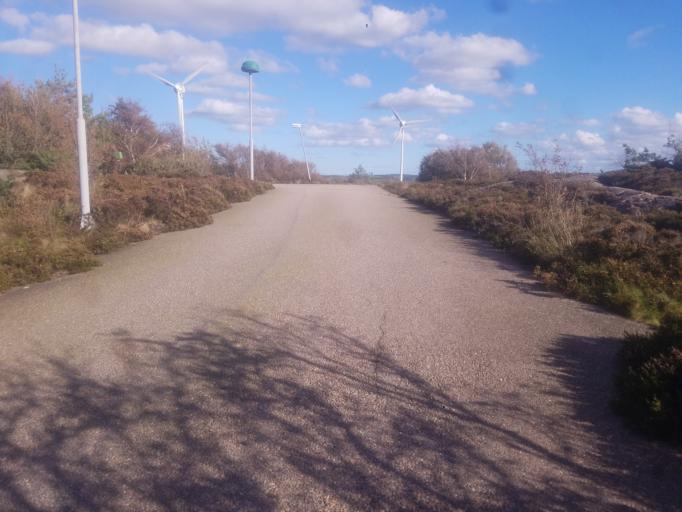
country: SE
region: Vaestra Goetaland
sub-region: Lysekils Kommun
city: Lysekil
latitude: 58.3383
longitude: 11.4102
